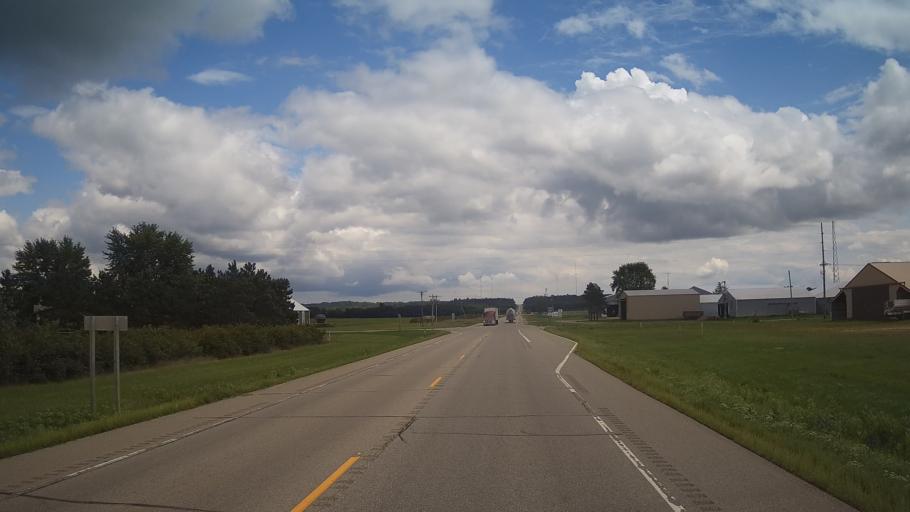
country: US
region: Wisconsin
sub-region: Marquette County
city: Westfield
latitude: 44.0221
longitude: -89.6000
